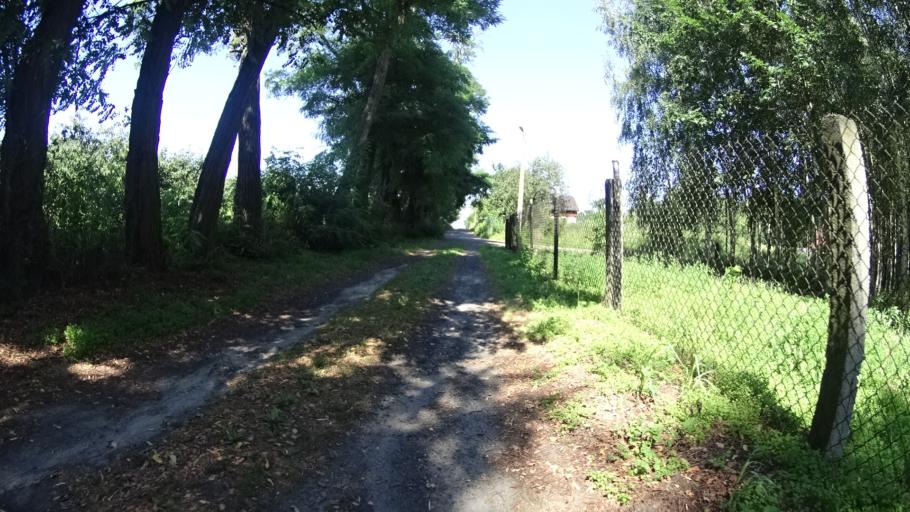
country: PL
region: Masovian Voivodeship
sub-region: Powiat bialobrzeski
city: Bialobrzegi
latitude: 51.6679
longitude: 20.8845
